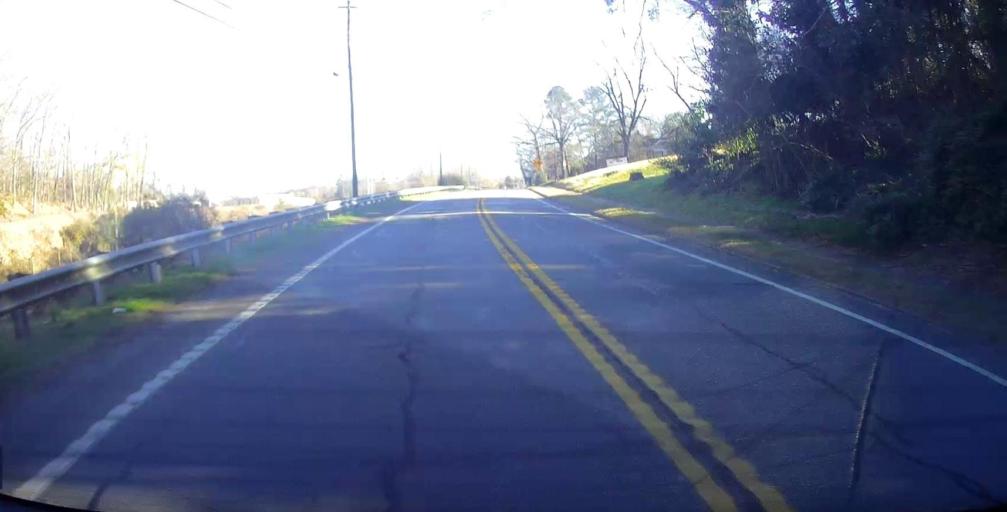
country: US
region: Georgia
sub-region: Talbot County
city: Sardis
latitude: 32.7892
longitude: -84.5628
